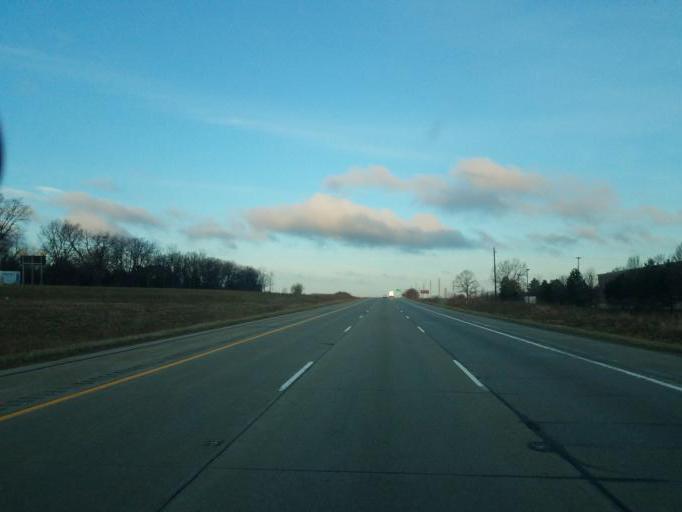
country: US
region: Michigan
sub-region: Livingston County
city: Howell
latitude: 42.5795
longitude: -83.8605
